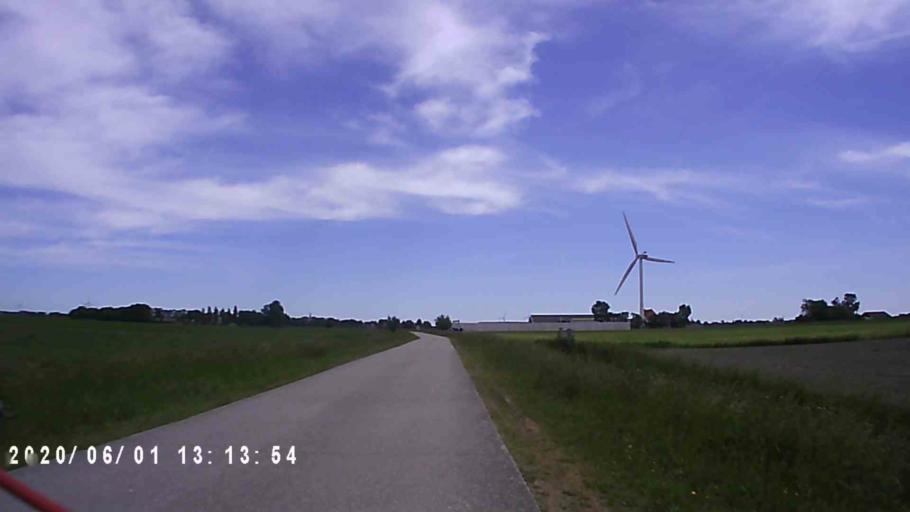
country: NL
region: Friesland
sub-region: Gemeente Littenseradiel
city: Wommels
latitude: 53.1185
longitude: 5.5547
